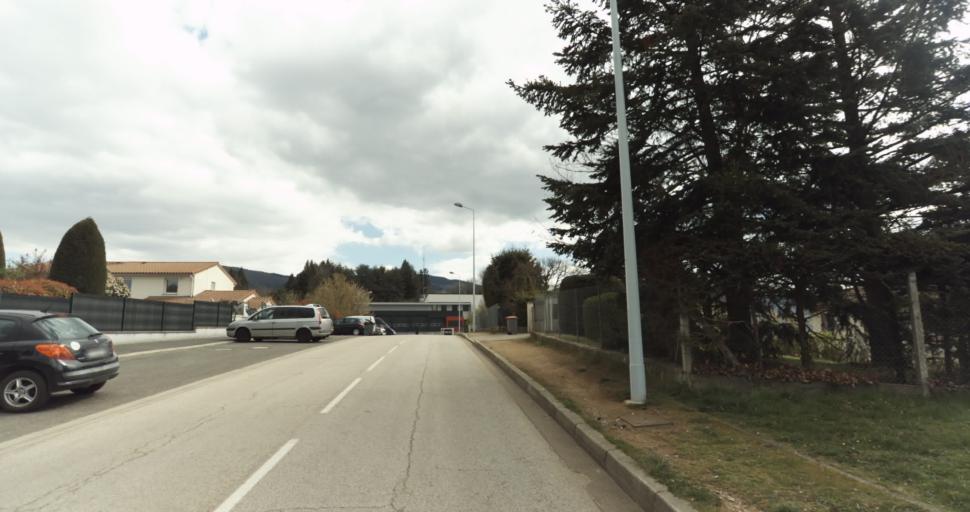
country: FR
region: Rhone-Alpes
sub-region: Departement de la Loire
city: Saint-Jean-Bonnefonds
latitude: 45.4441
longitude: 4.4402
